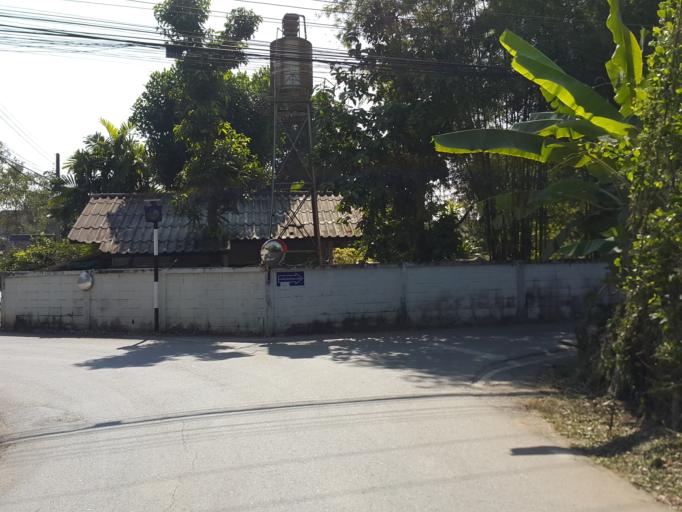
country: TH
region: Chiang Mai
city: Chiang Mai
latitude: 18.8188
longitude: 99.0067
